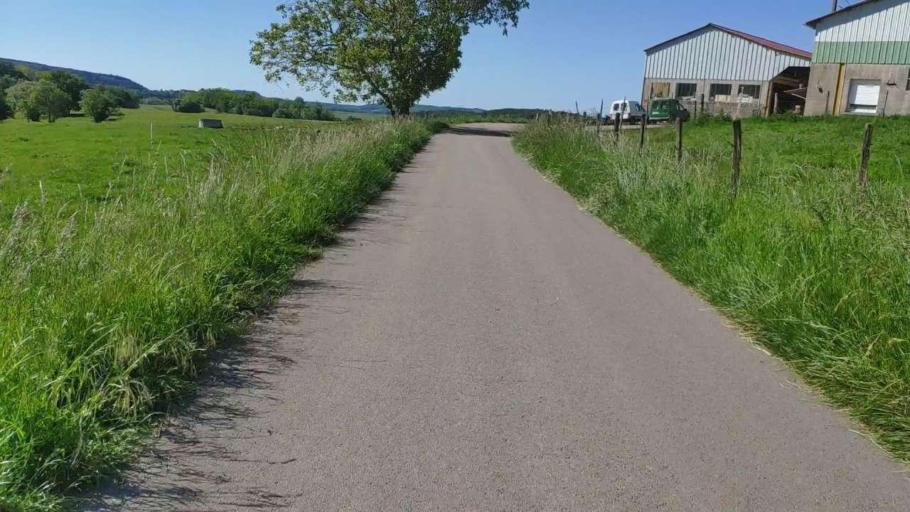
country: FR
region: Franche-Comte
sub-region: Departement du Jura
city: Perrigny
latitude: 46.7223
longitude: 5.5735
